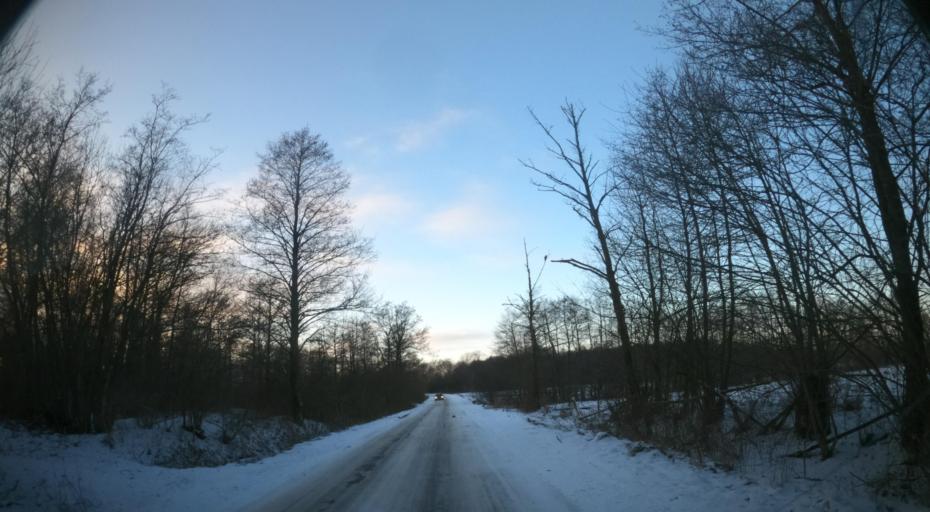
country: PL
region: West Pomeranian Voivodeship
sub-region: Powiat slawienski
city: Darlowo
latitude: 54.2990
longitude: 16.4012
